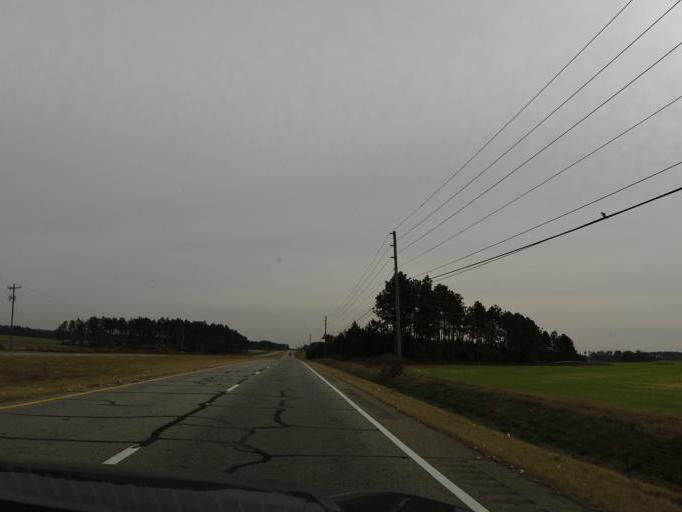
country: US
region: Georgia
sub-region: Decatur County
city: Bainbridge
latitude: 30.9651
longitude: -84.7252
